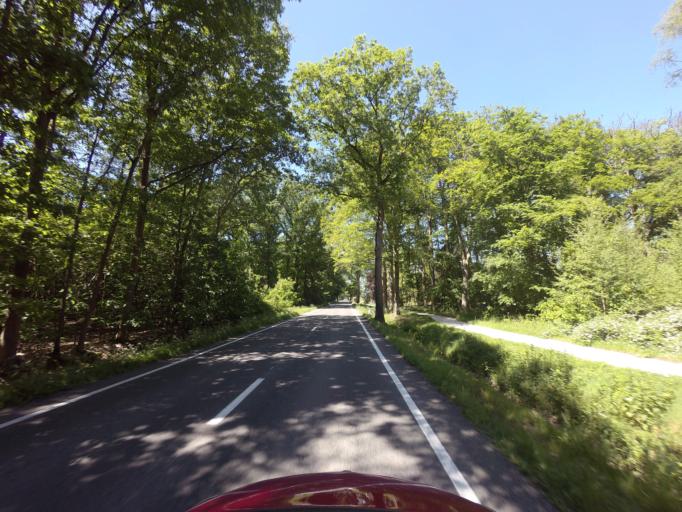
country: BE
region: Flanders
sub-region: Provincie Antwerpen
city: Arendonk
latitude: 51.3607
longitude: 5.0564
